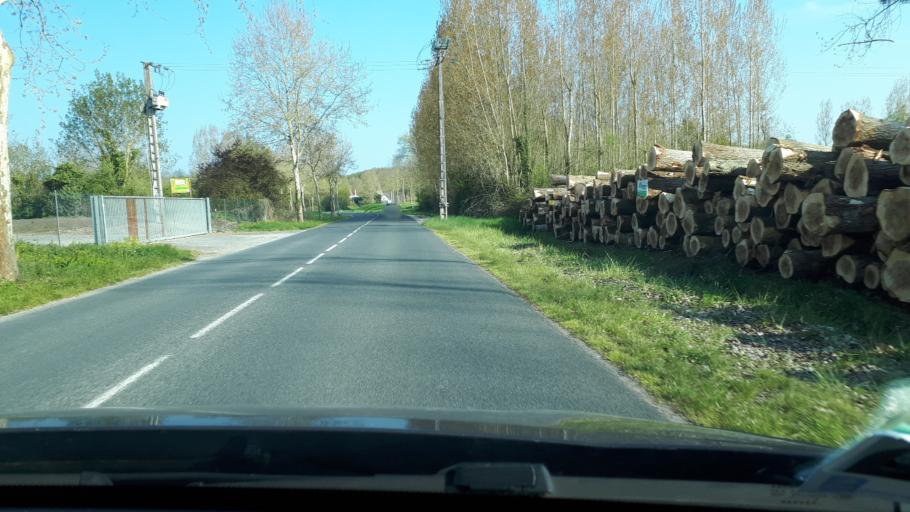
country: FR
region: Centre
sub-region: Departement d'Indre-et-Loire
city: La Croix-en-Touraine
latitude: 47.3379
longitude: 0.9845
